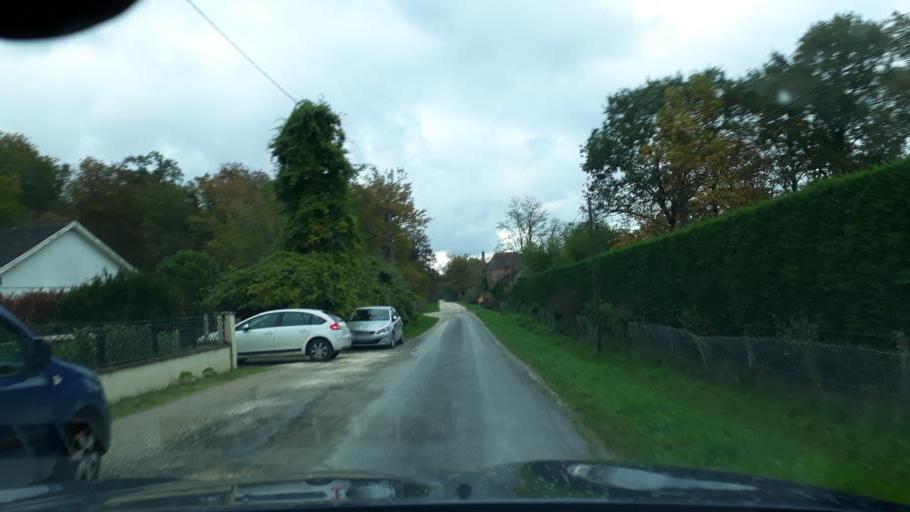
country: FR
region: Centre
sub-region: Departement du Loiret
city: Bray-en-Val
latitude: 47.8197
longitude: 2.4121
